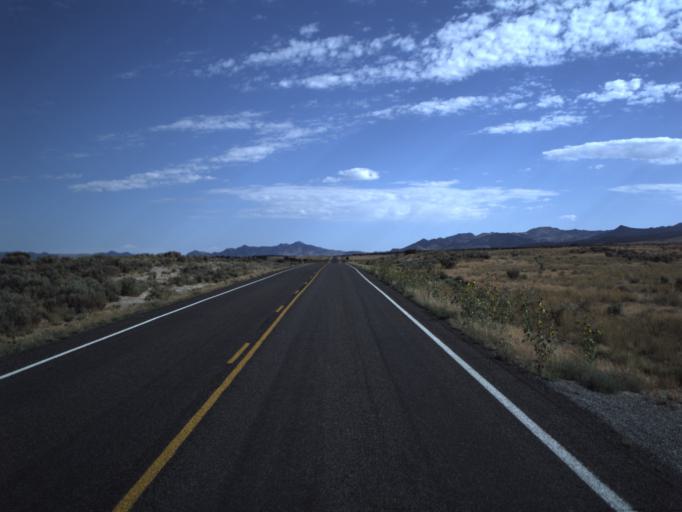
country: US
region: Utah
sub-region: Juab County
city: Mona
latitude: 39.7220
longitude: -112.1982
